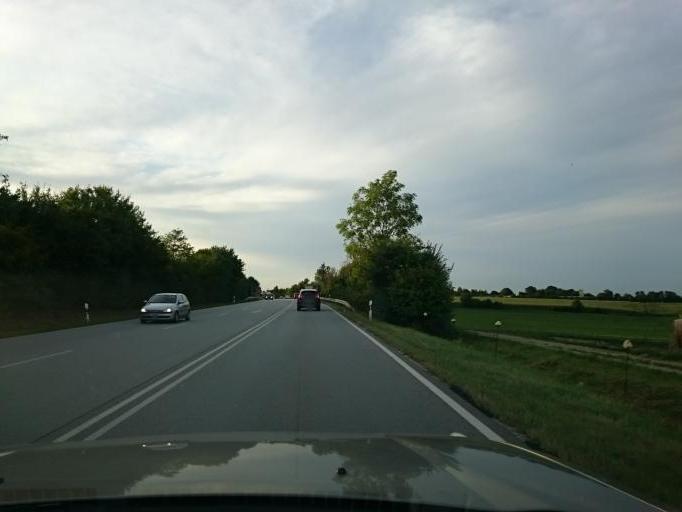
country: DE
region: Bavaria
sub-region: Lower Bavaria
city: Landau an der Isar
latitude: 48.6530
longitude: 12.7065
